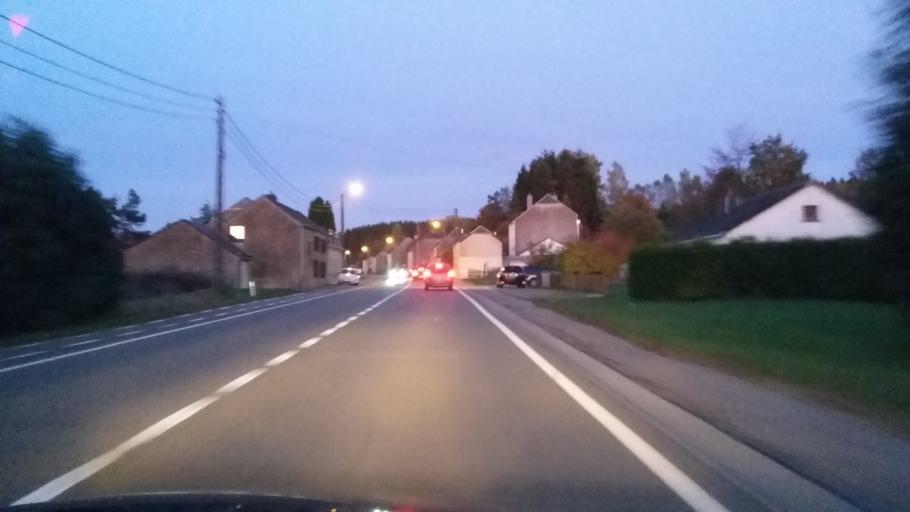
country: BE
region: Wallonia
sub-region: Province du Luxembourg
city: Saint-Leger
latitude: 49.6820
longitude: 5.7108
